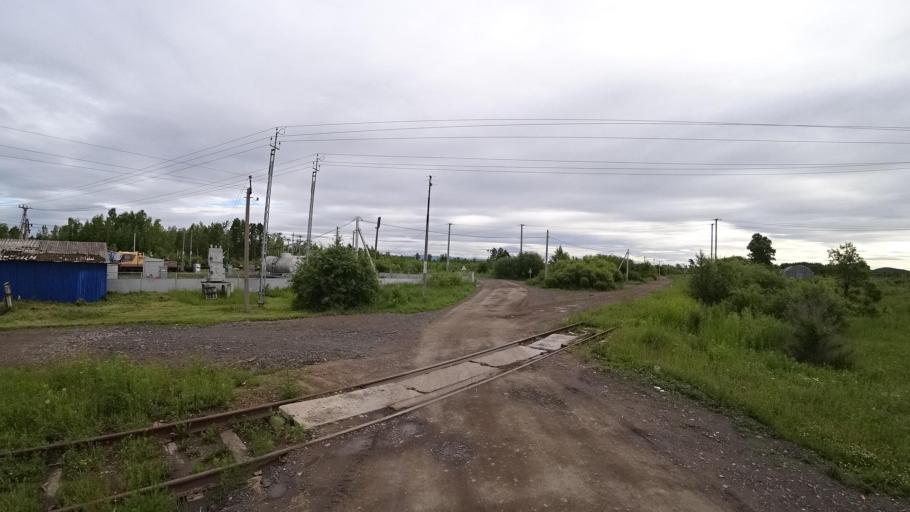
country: RU
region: Khabarovsk Krai
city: Amursk
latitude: 49.9045
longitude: 136.1436
